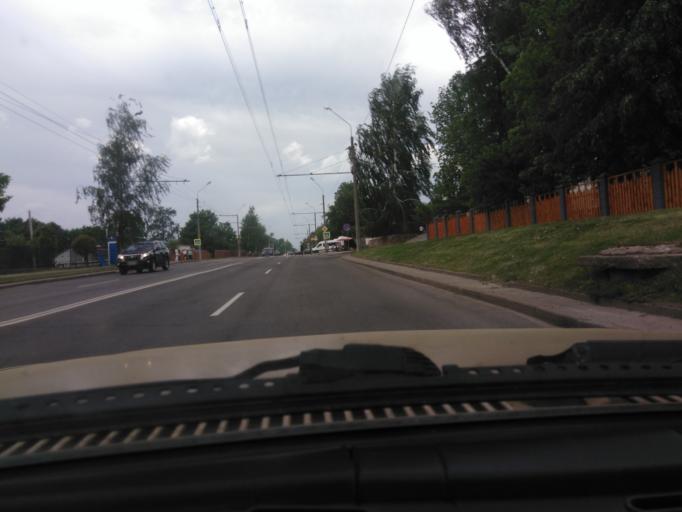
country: BY
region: Mogilev
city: Mahilyow
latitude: 53.9316
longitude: 30.3370
